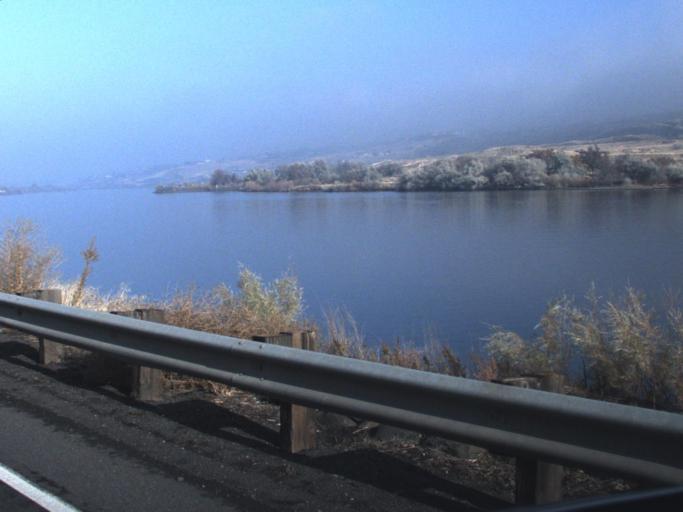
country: US
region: Washington
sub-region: Asotin County
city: Asotin
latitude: 46.3633
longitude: -117.0650
